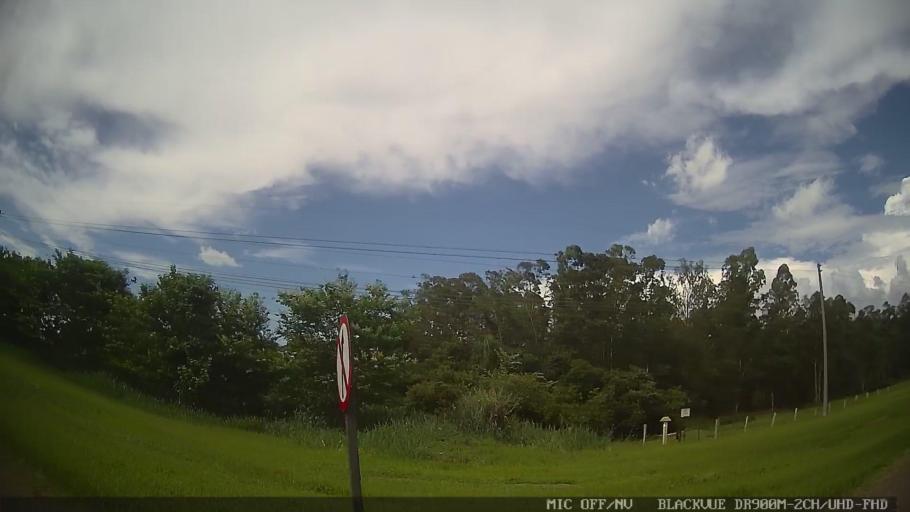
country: BR
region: Sao Paulo
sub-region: Conchas
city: Conchas
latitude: -23.0261
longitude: -47.9931
